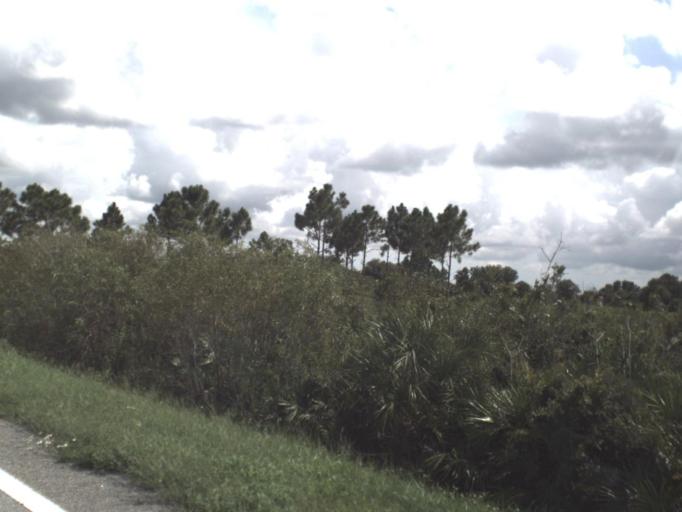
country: US
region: Florida
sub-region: Sarasota County
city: Warm Mineral Springs
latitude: 27.2052
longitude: -82.2460
